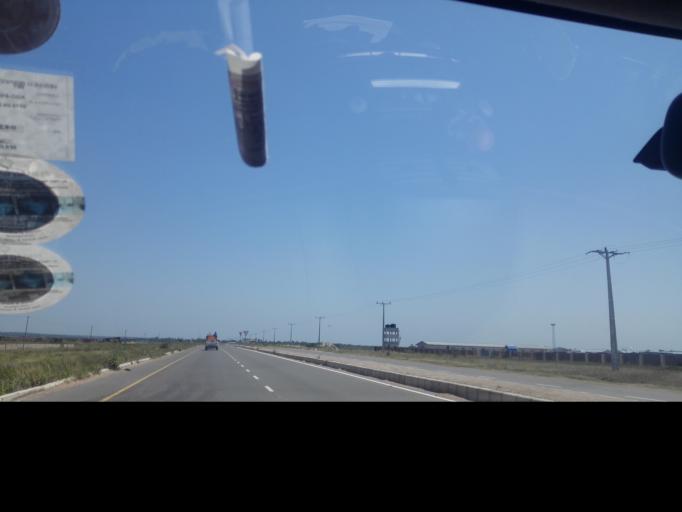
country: MZ
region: Maputo City
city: Maputo
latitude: -25.8370
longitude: 32.6718
